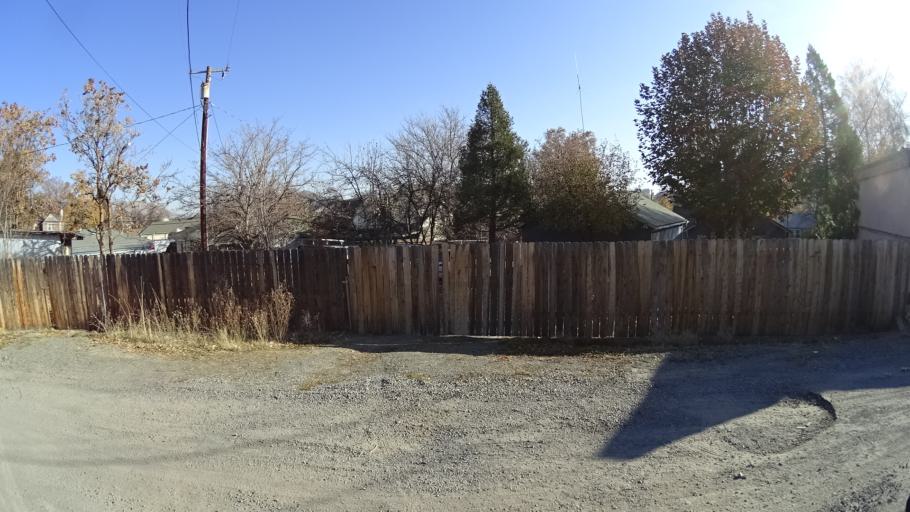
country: US
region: California
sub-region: Siskiyou County
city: Yreka
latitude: 41.7383
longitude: -122.6346
